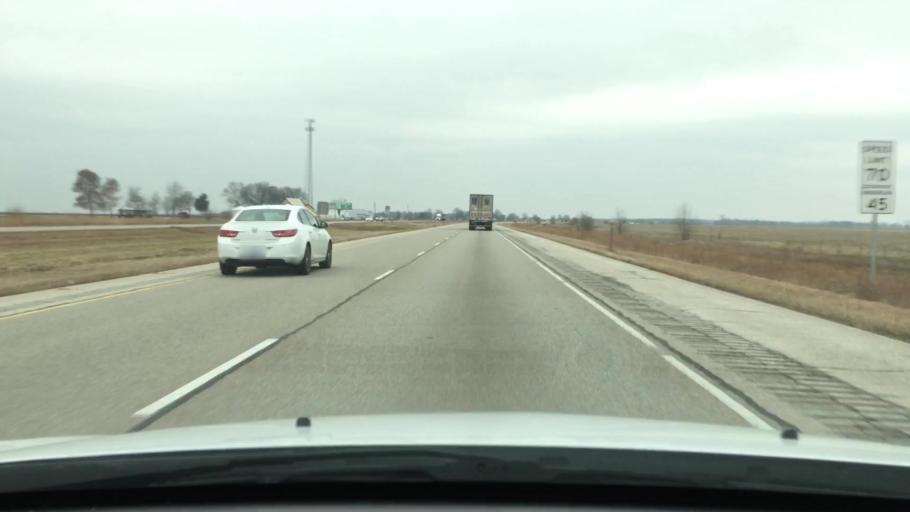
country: US
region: Illinois
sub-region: Logan County
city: Atlanta
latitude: 40.3210
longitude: -89.1572
